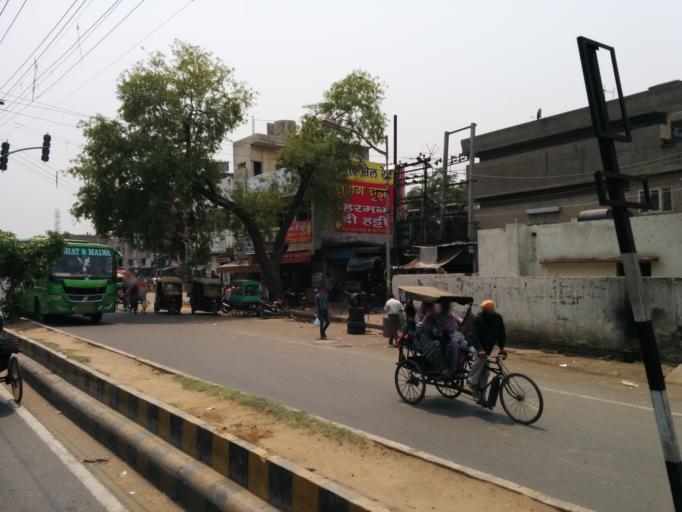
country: IN
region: Punjab
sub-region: Amritsar
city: Amritsar
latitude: 31.6280
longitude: 74.8825
